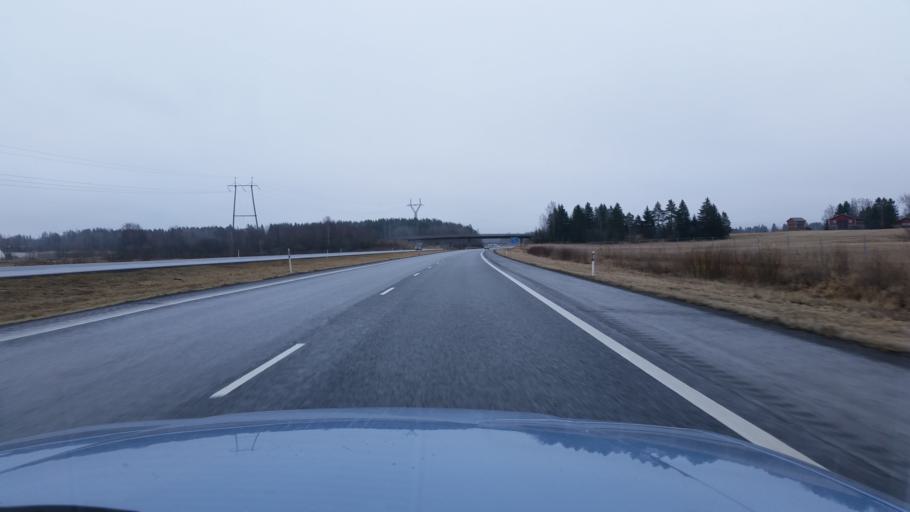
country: FI
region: Pirkanmaa
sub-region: Etelae-Pirkanmaa
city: Akaa
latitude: 61.1722
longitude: 23.9295
